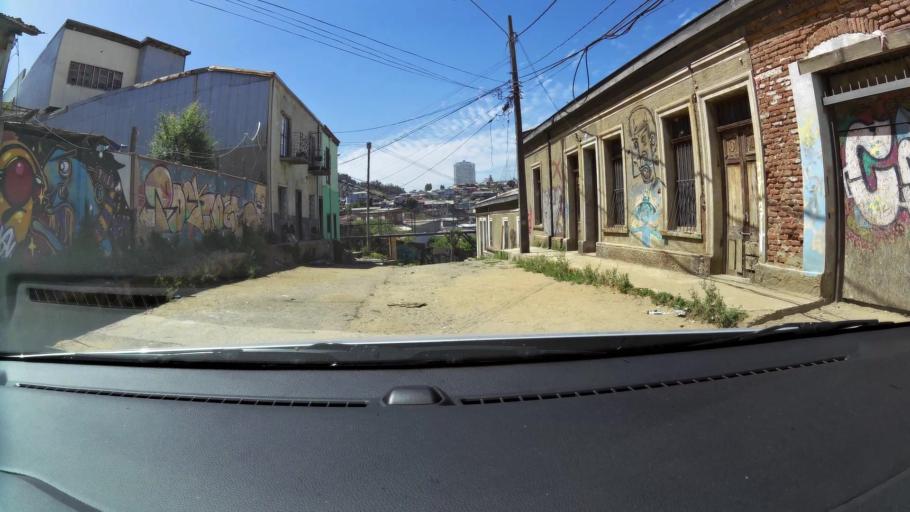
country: CL
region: Valparaiso
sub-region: Provincia de Valparaiso
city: Valparaiso
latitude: -33.0499
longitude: -71.5989
